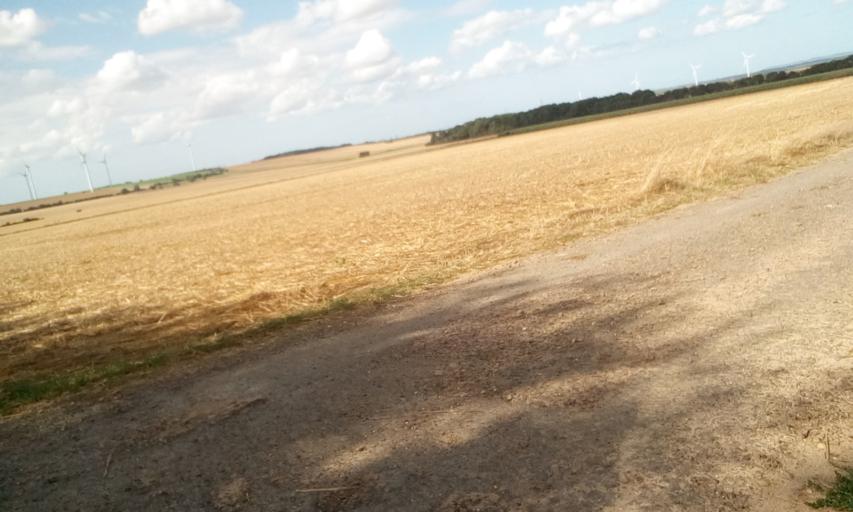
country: FR
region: Lower Normandy
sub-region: Departement du Calvados
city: Saint-Sylvain
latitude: 49.0720
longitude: -0.2472
